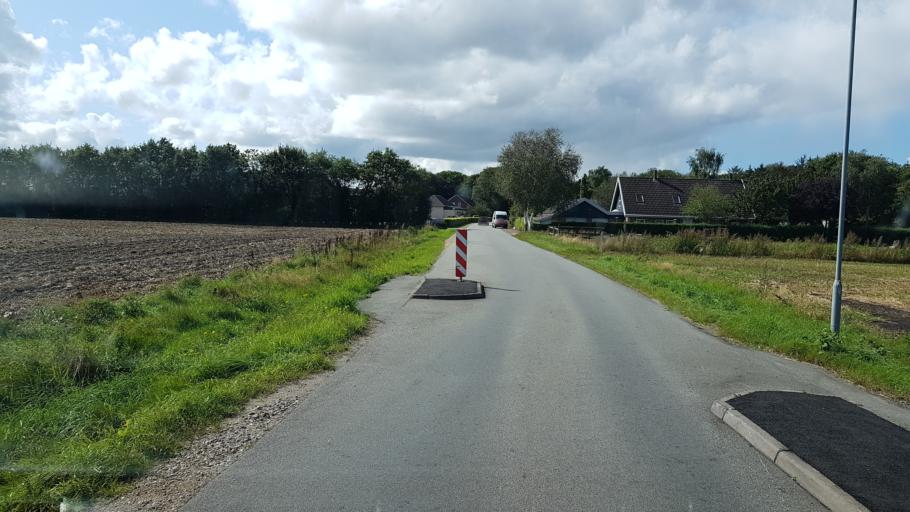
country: DK
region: South Denmark
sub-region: Esbjerg Kommune
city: Bramming
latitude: 55.6164
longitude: 8.7302
